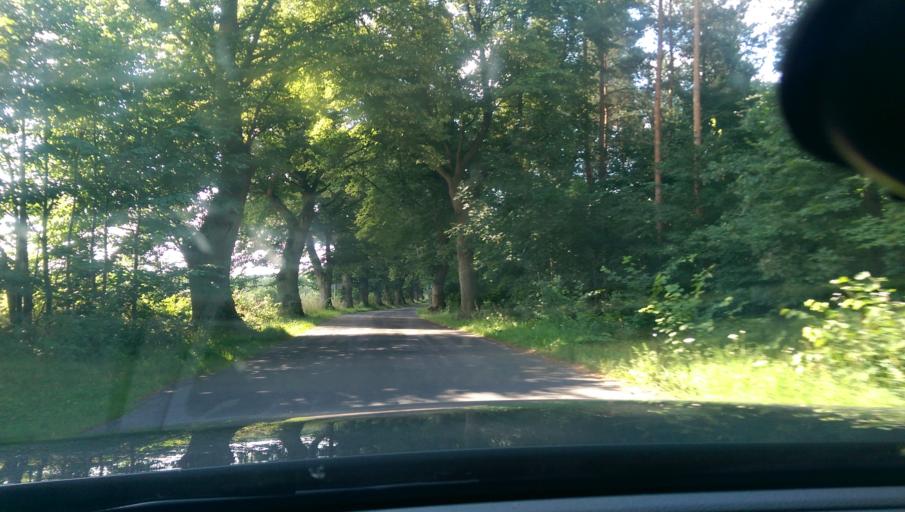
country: PL
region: West Pomeranian Voivodeship
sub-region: Powiat walecki
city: Walcz
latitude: 53.3735
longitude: 16.5042
